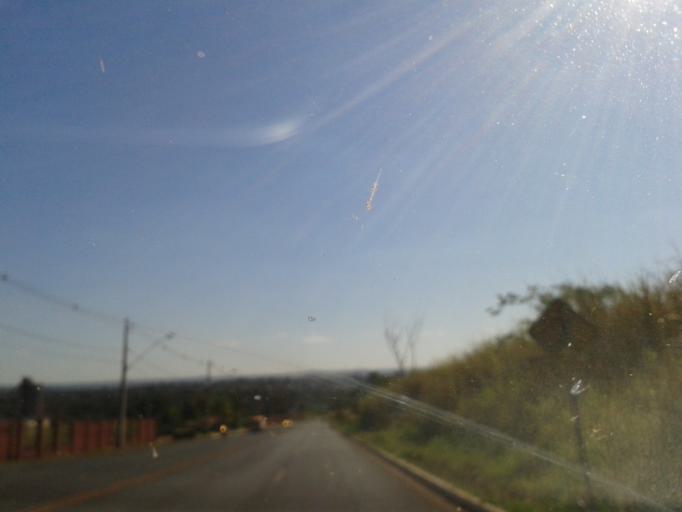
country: BR
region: Goias
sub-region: Itumbiara
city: Itumbiara
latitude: -18.4277
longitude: -49.1988
